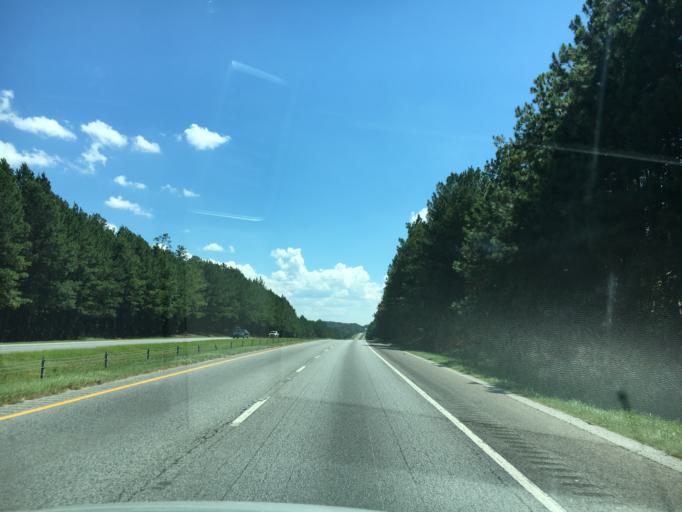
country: US
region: South Carolina
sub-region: Spartanburg County
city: Woodruff
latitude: 34.7751
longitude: -81.9537
